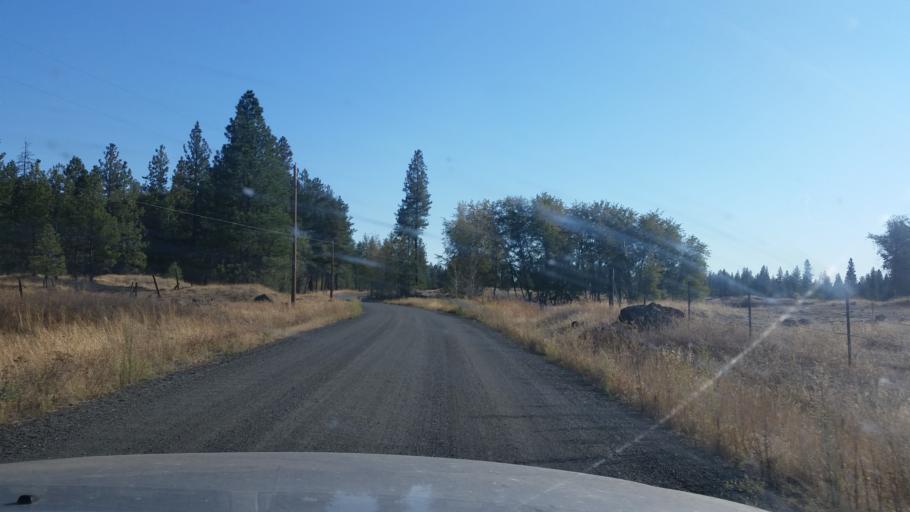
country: US
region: Washington
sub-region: Spokane County
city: Cheney
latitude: 47.4252
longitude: -117.6507
